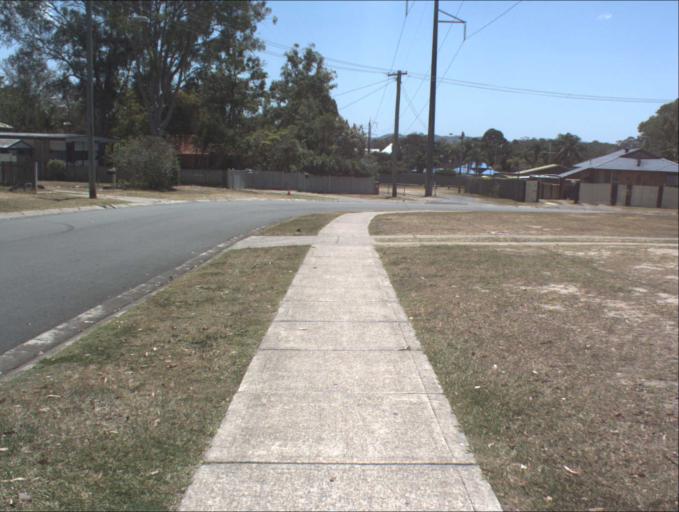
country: AU
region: Queensland
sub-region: Logan
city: Beenleigh
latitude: -27.7054
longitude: 153.2097
